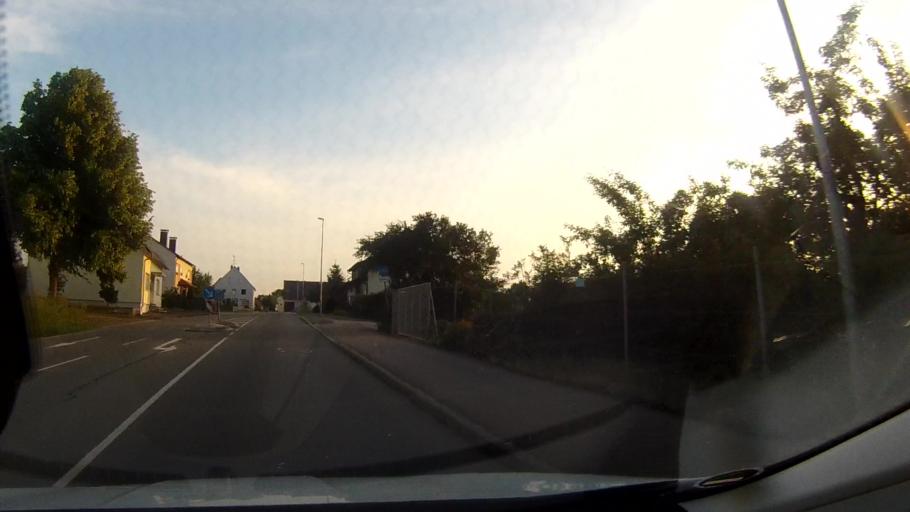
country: DE
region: Baden-Wuerttemberg
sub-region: Tuebingen Region
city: Staig
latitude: 48.2935
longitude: 9.9770
